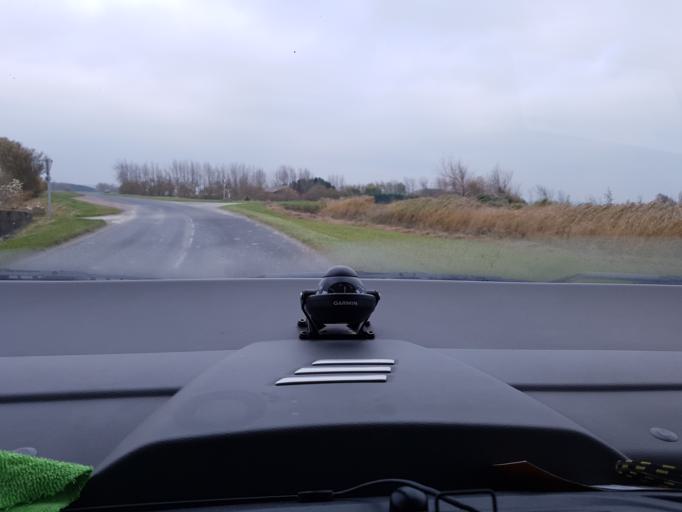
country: FR
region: Picardie
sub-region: Departement de la Somme
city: Cayeux-sur-Mer
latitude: 50.1598
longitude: 1.4951
